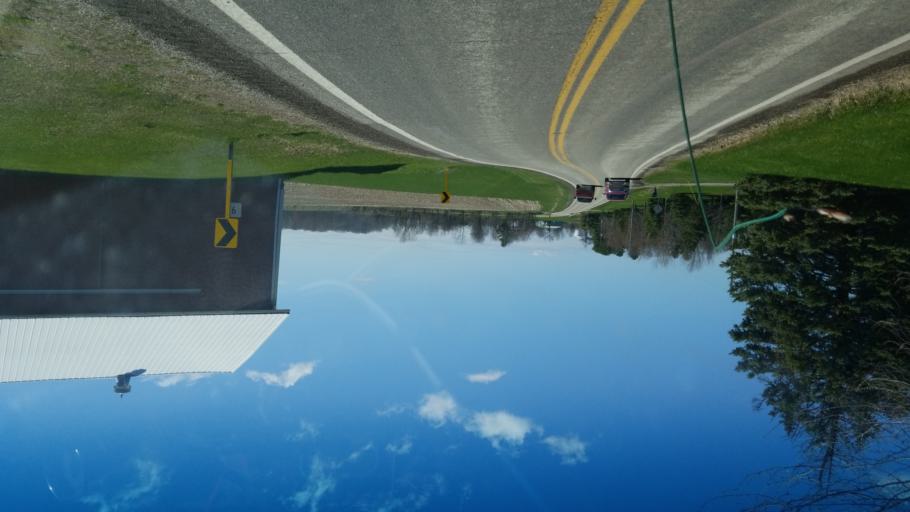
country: US
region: Ohio
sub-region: Crawford County
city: Crestline
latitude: 40.8620
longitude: -82.7671
